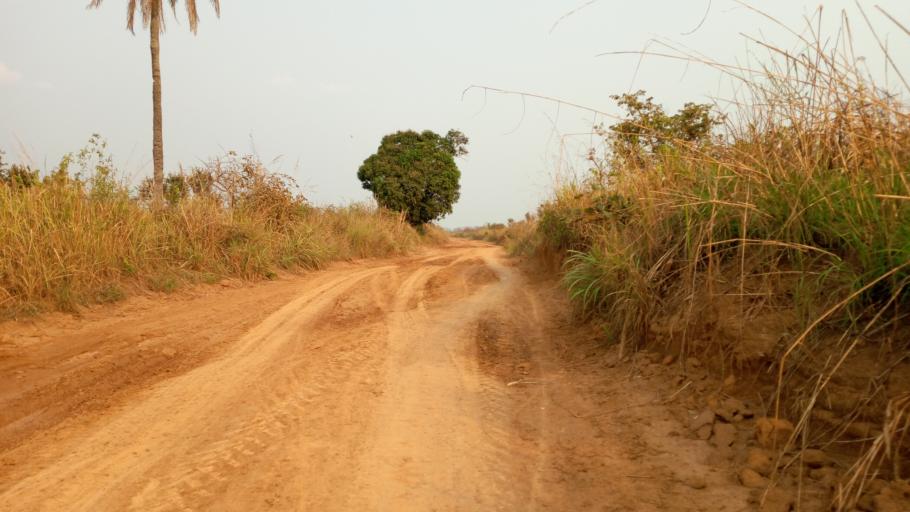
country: CD
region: Bandundu
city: Bandundu
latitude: -3.4074
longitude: 17.5937
